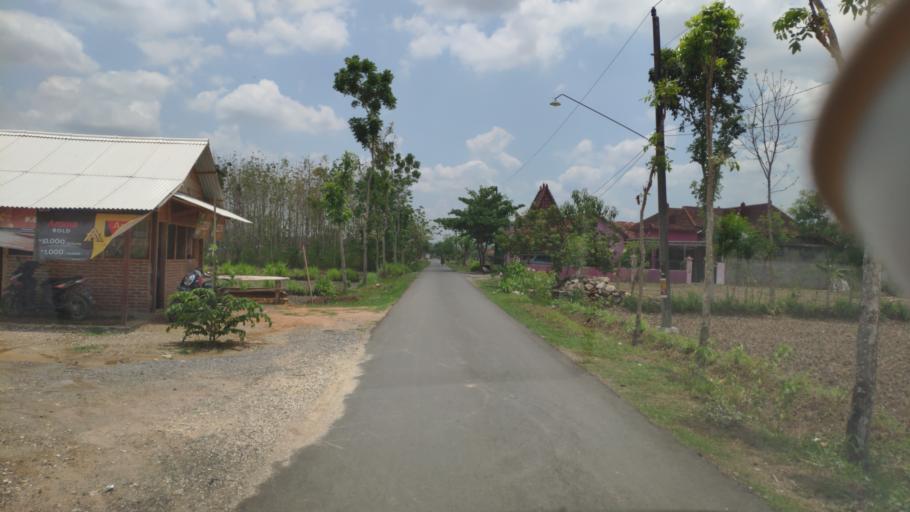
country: ID
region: Central Java
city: Mojo Wetan
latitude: -7.0314
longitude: 111.3710
